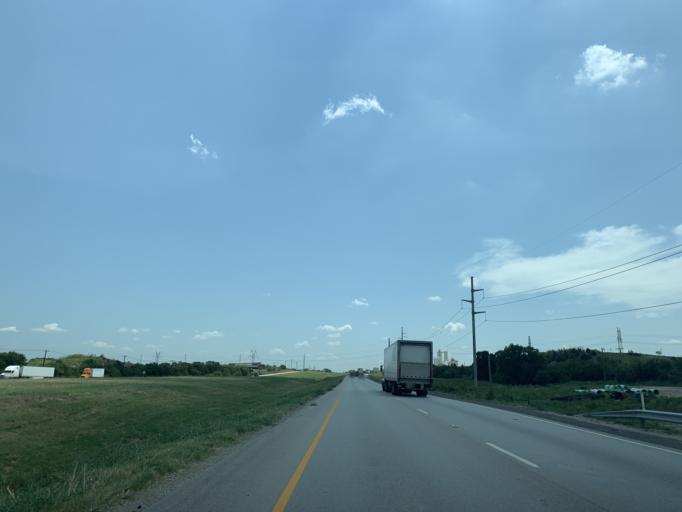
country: US
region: Texas
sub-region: Denton County
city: Roanoke
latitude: 33.0198
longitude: -97.2474
